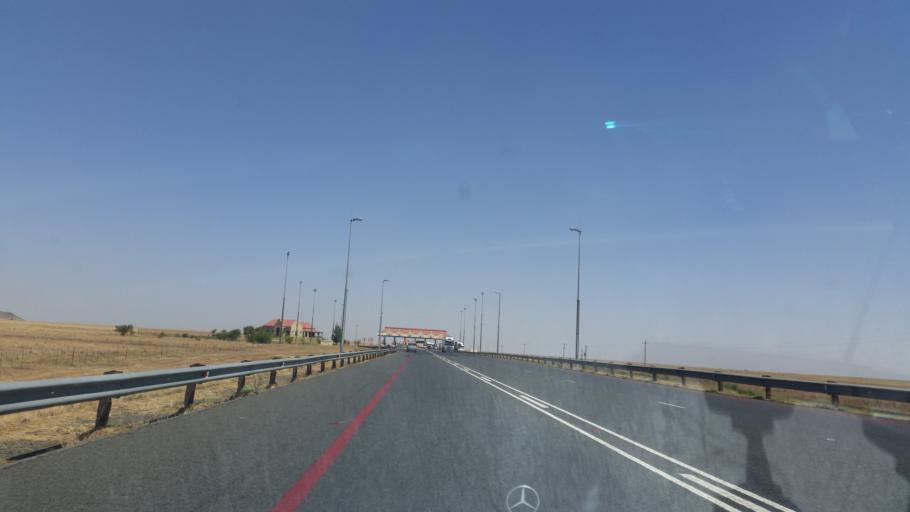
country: ZA
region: Orange Free State
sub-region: Lejweleputswa District Municipality
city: Brandfort
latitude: -28.7965
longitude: 26.6935
